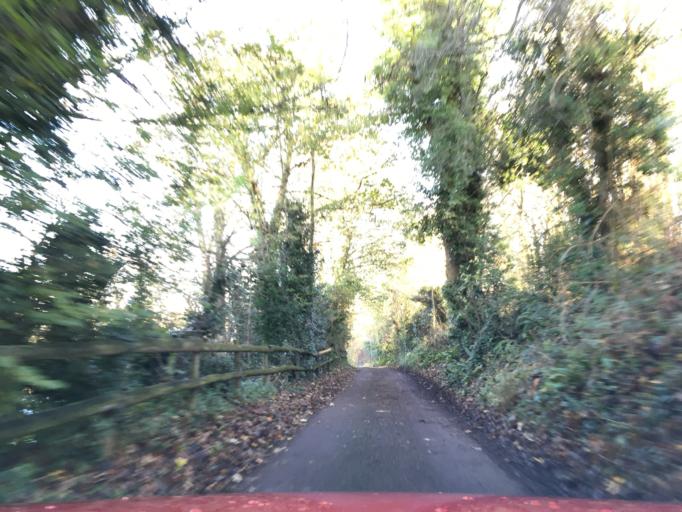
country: GB
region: England
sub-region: South Gloucestershire
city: Tytherington
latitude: 51.6046
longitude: -2.4963
